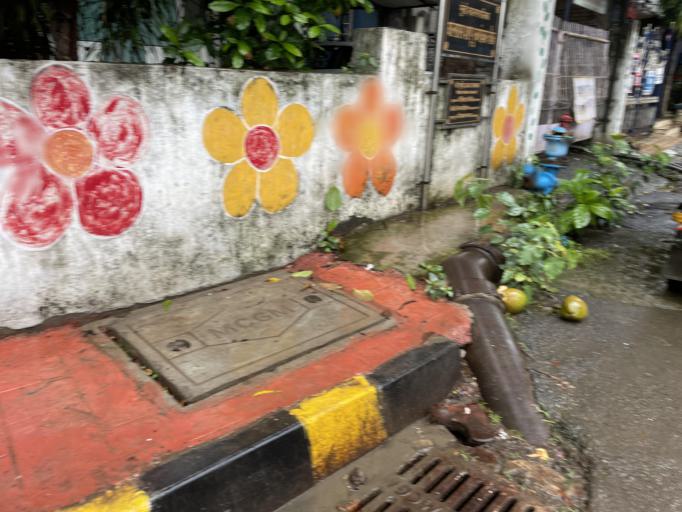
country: IN
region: Maharashtra
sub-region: Mumbai Suburban
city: Borivli
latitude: 19.2529
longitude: 72.8626
